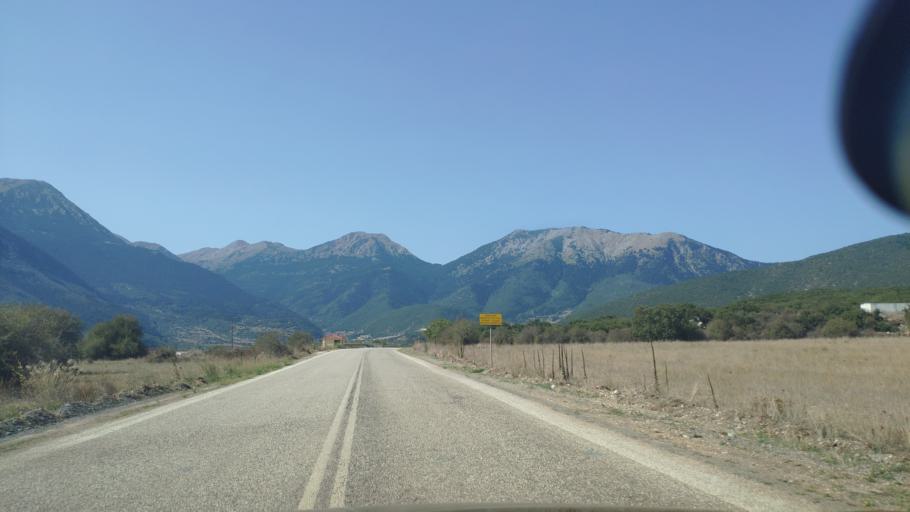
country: GR
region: Peloponnese
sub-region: Nomos Korinthias
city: Nemea
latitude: 37.8503
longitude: 22.4332
